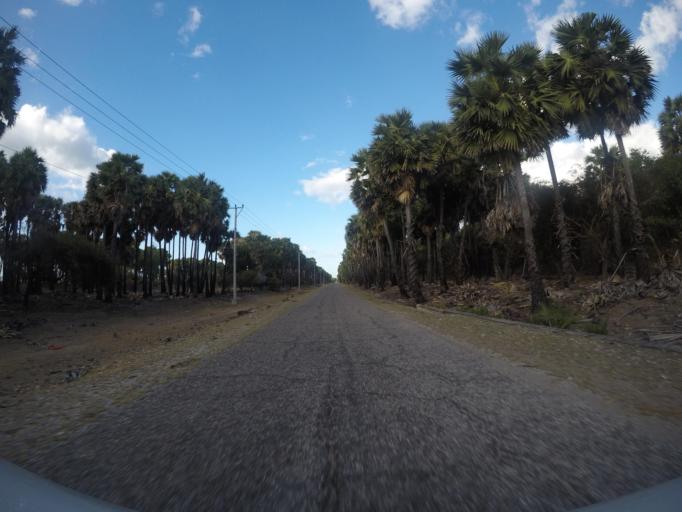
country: TL
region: Lautem
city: Lospalos
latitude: -8.3414
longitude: 126.9317
